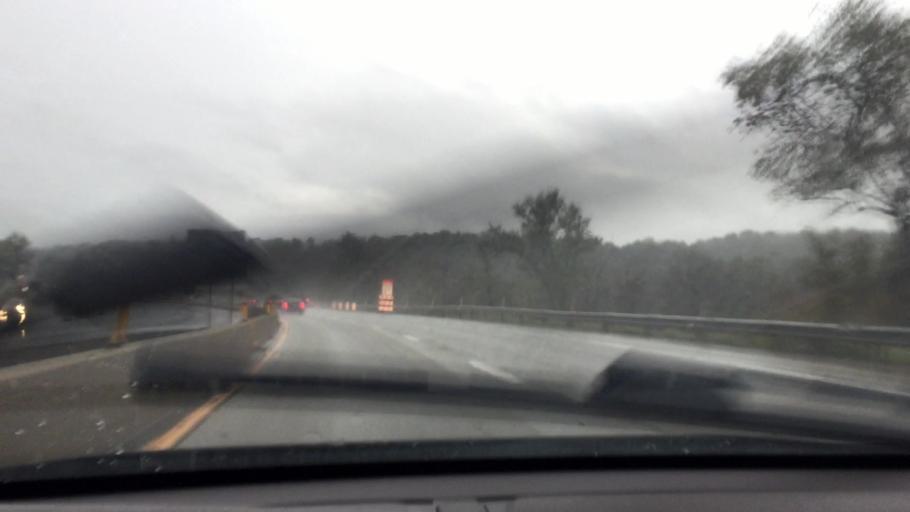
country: US
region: Pennsylvania
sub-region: Washington County
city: East Washington
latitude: 40.1680
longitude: -80.1772
